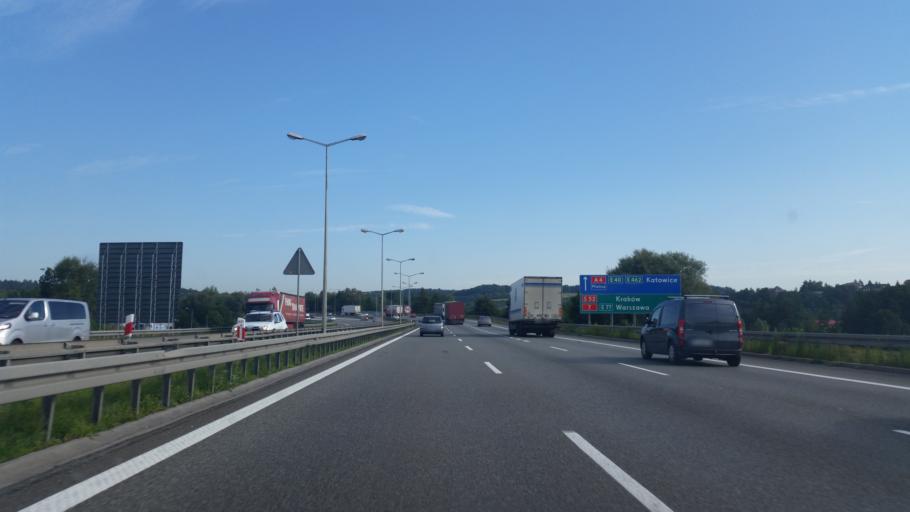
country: PL
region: Lesser Poland Voivodeship
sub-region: Powiat krakowski
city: Balice
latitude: 50.0823
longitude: 19.8083
